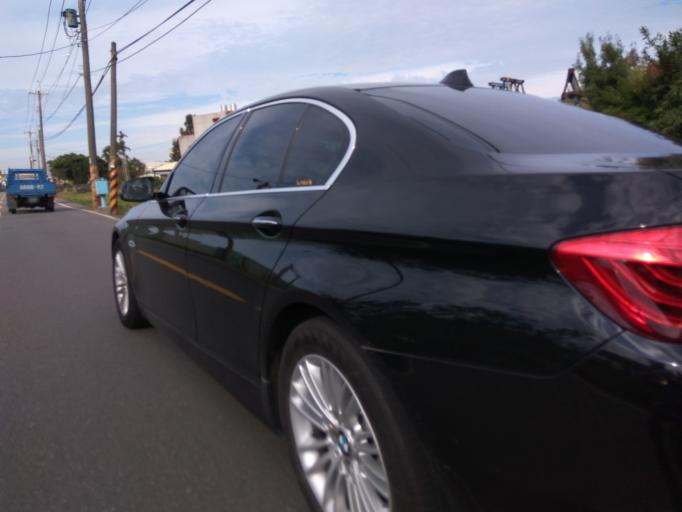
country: TW
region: Taiwan
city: Taoyuan City
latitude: 24.9505
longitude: 121.1368
